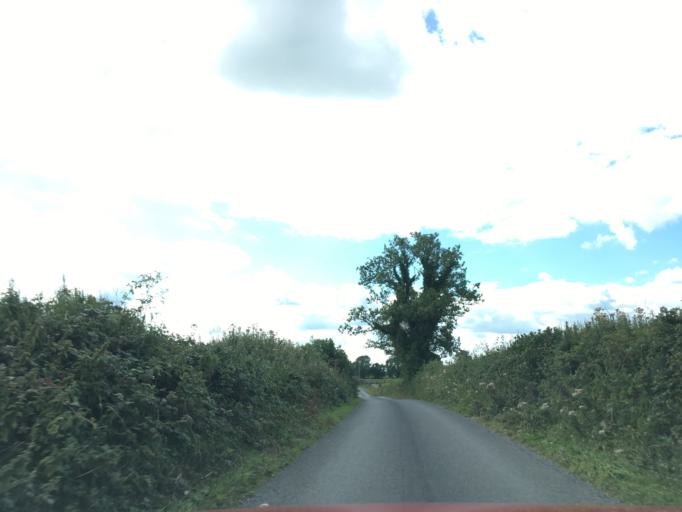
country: IE
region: Munster
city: Cashel
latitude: 52.4957
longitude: -7.9118
